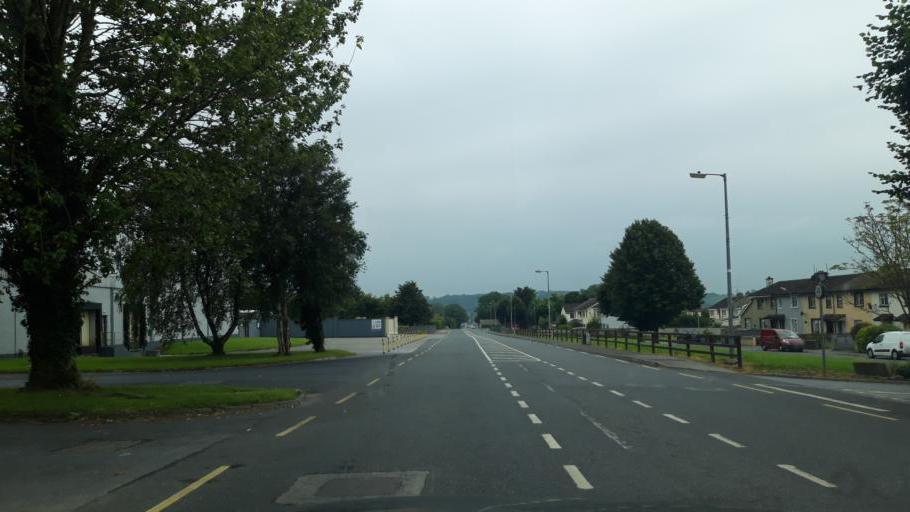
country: IE
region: Munster
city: Fethard
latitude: 52.4737
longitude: -7.6919
